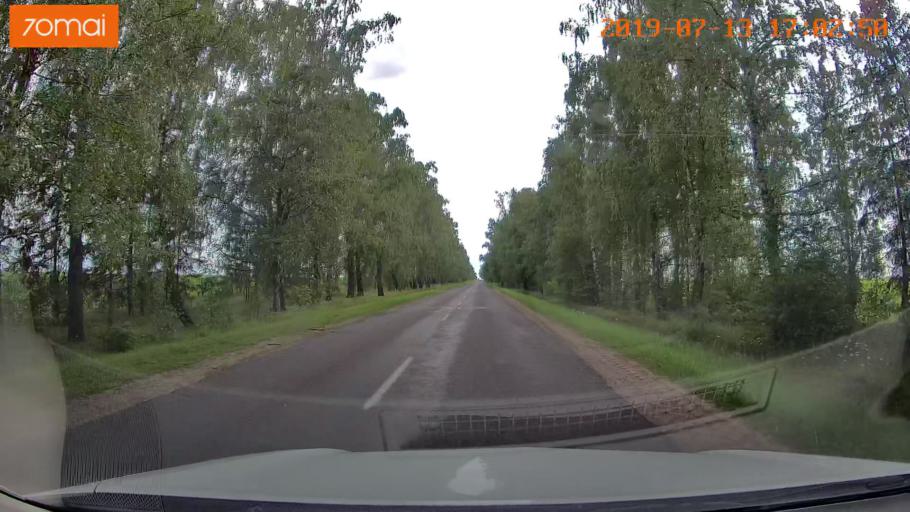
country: BY
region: Mogilev
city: Kirawsk
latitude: 53.2820
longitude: 29.3830
